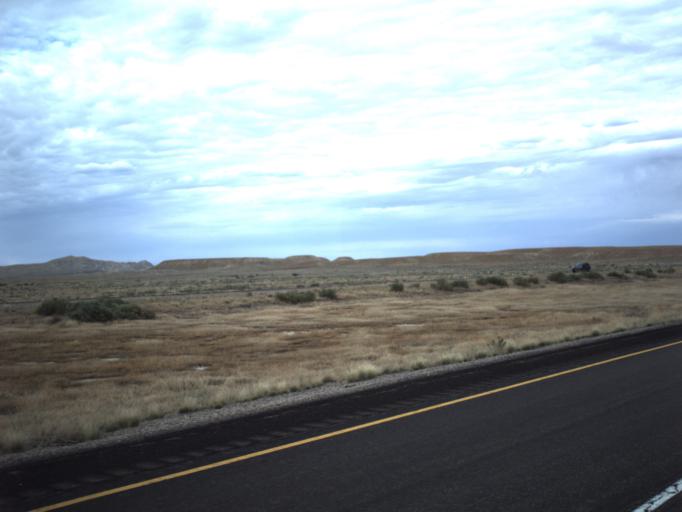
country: US
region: Utah
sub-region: Grand County
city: Moab
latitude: 38.9442
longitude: -109.6451
